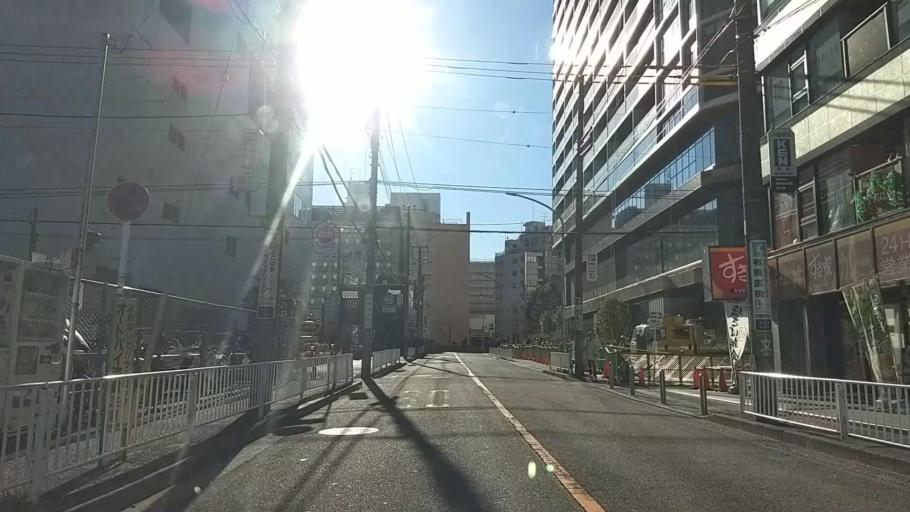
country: JP
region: Kanagawa
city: Yokohama
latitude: 35.4663
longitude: 139.6165
